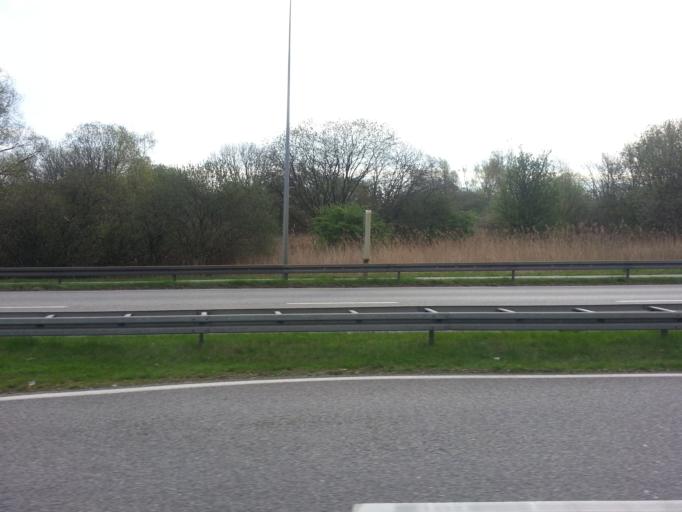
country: DE
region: Mecklenburg-Vorpommern
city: Lambrechtshagen
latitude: 54.1165
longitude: 12.0658
